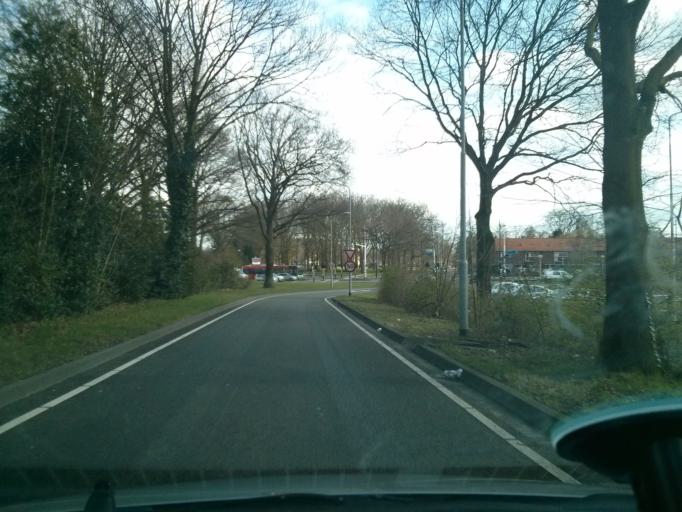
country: NL
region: North Brabant
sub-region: Gemeente Eindhoven
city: Meerhoven
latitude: 51.4442
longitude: 5.4413
